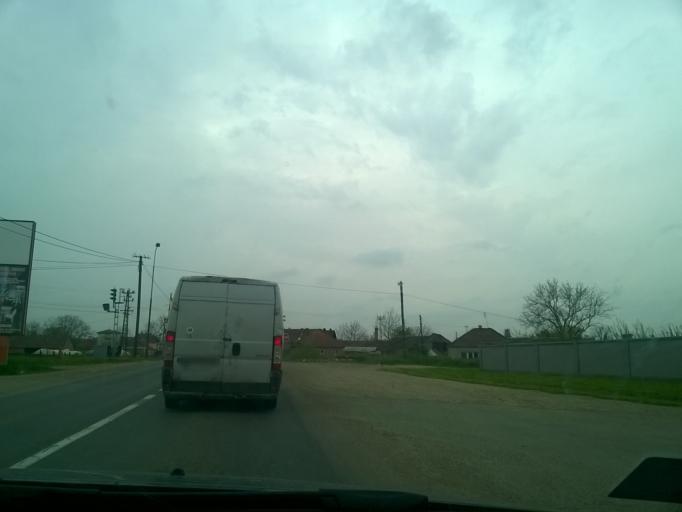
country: RS
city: Platicevo
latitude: 44.8293
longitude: 19.7773
